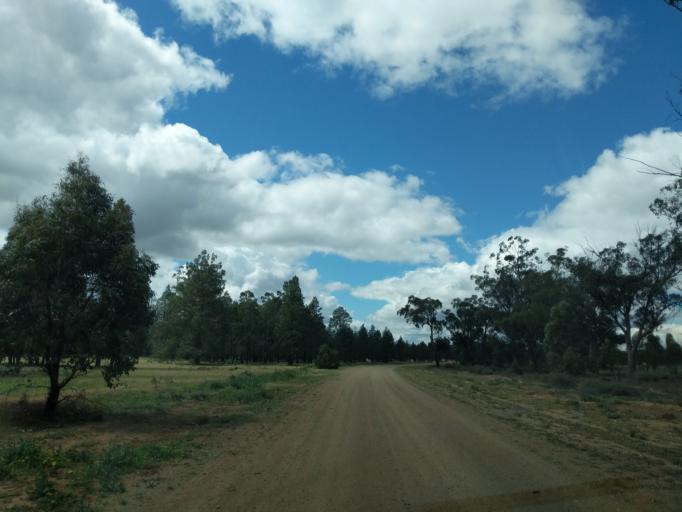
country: AU
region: New South Wales
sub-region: Coolamon
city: Coolamon
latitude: -34.8551
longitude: 146.9126
